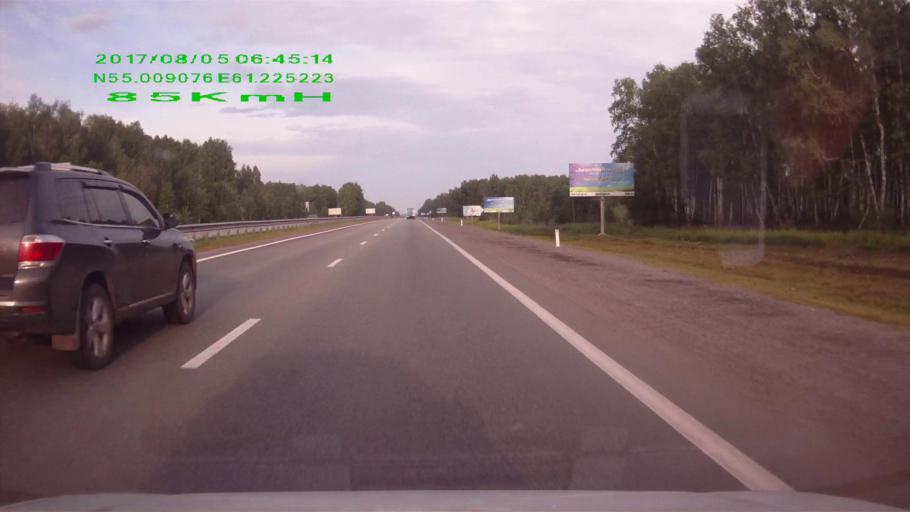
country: RU
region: Chelyabinsk
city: Sargazy
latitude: 55.0090
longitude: 61.2246
